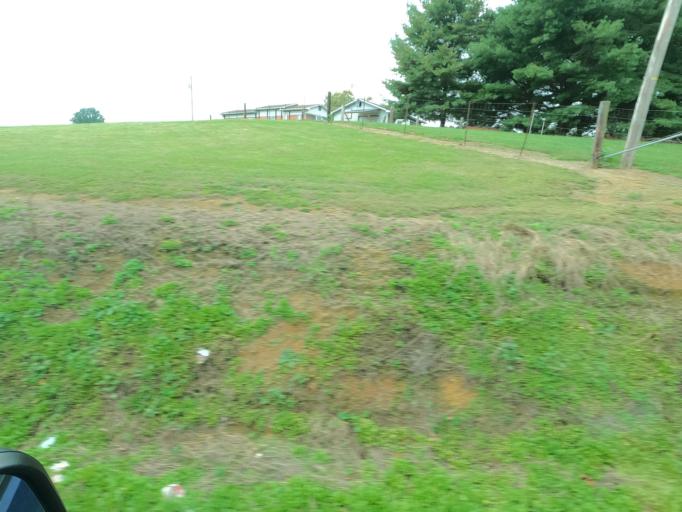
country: US
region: Tennessee
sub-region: Washington County
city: Jonesborough
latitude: 36.2537
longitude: -82.5422
